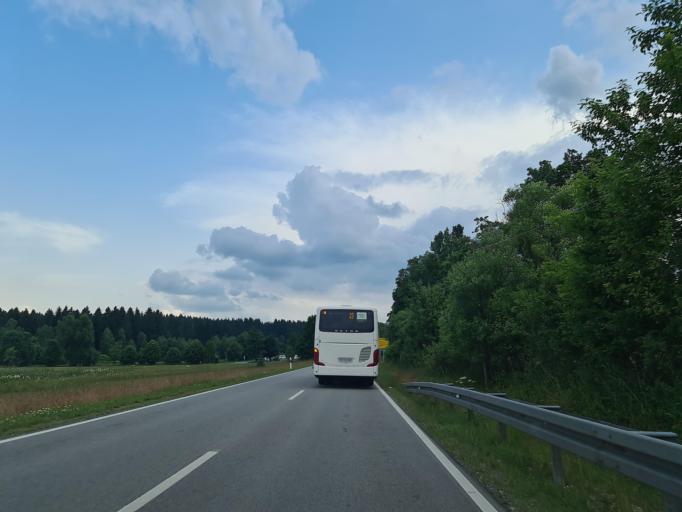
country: DE
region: Saxony
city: Hammerbrucke
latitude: 50.4183
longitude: 12.4004
